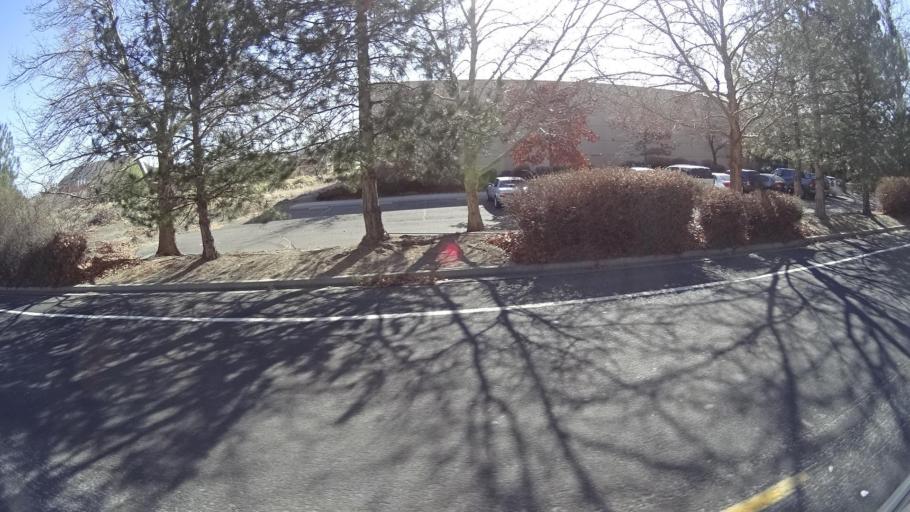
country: US
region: Nevada
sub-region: Washoe County
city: Sparks
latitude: 39.4611
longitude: -119.7768
